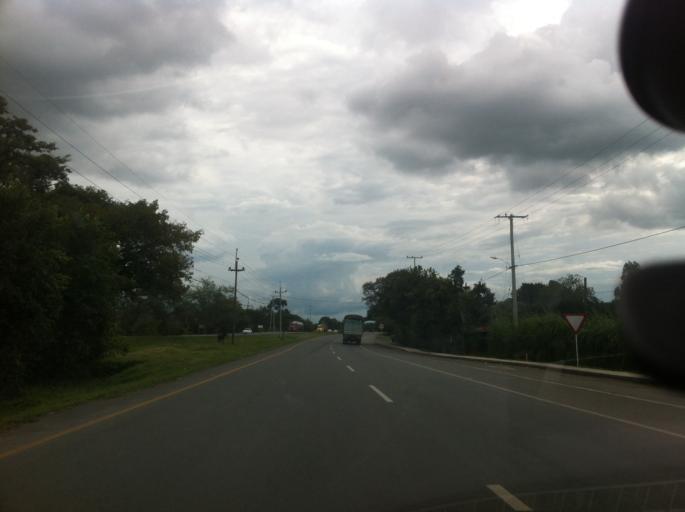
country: CO
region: Valle del Cauca
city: El Cerrito
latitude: 3.7103
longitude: -76.3196
